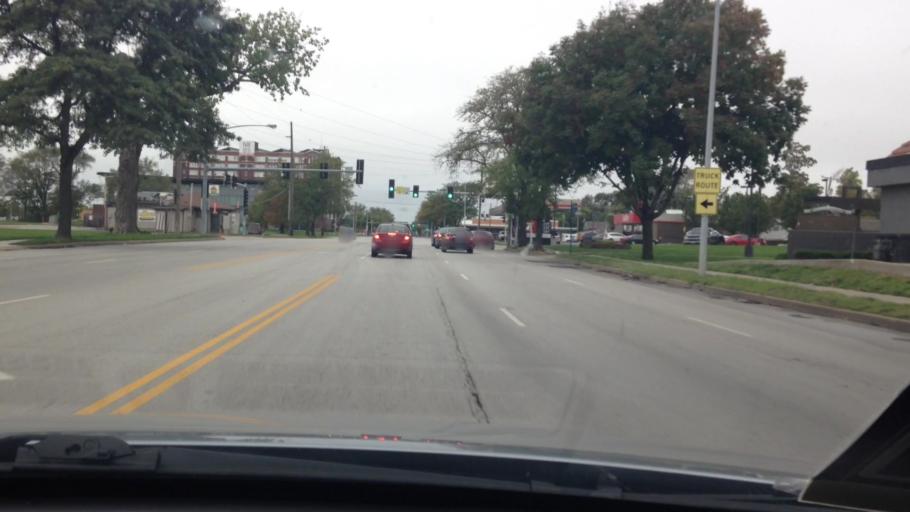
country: US
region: Missouri
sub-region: Clay County
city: North Kansas City
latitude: 39.1438
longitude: -94.5669
